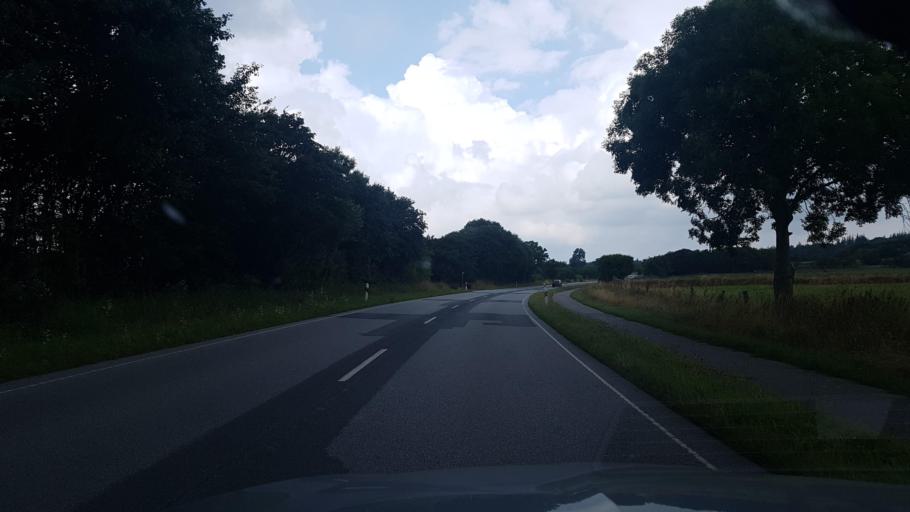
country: DE
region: Schleswig-Holstein
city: Schobull
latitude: 54.4983
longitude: 9.0216
